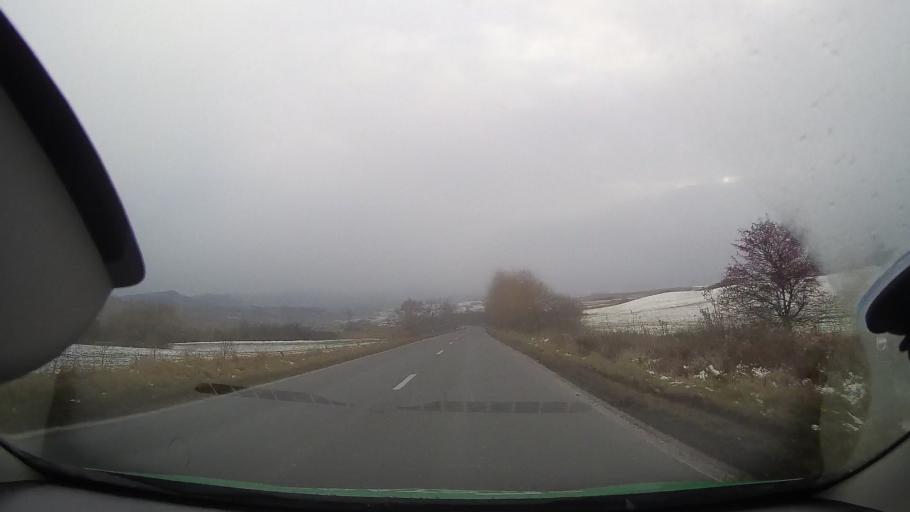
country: RO
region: Sibiu
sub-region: Comuna Blajel
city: Blajel
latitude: 46.2477
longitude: 24.3001
